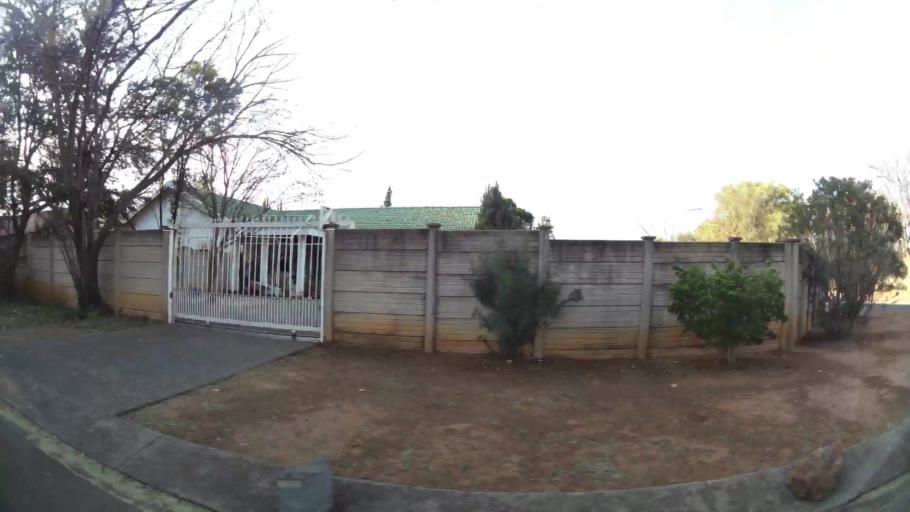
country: ZA
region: Orange Free State
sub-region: Mangaung Metropolitan Municipality
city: Bloemfontein
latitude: -29.1523
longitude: 26.1869
